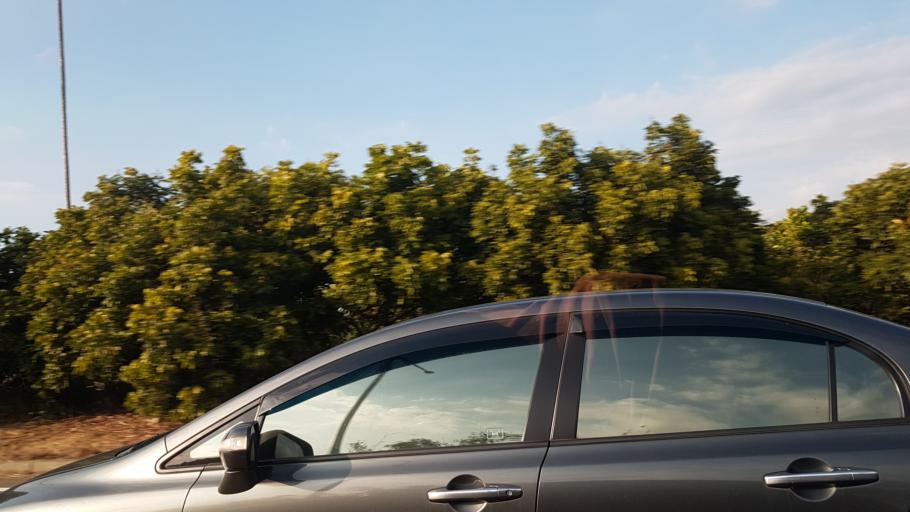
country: TW
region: Taiwan
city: Xinying
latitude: 23.3452
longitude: 120.4301
